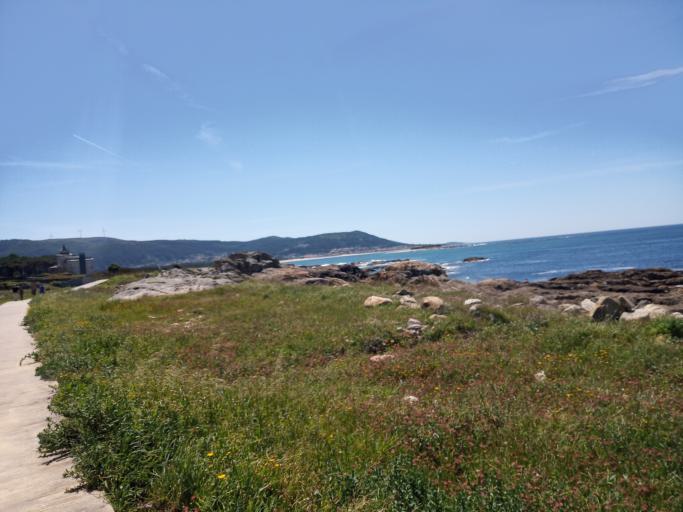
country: ES
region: Galicia
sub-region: Provincia de Pontevedra
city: A Guarda
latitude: 41.8748
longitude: -8.8760
